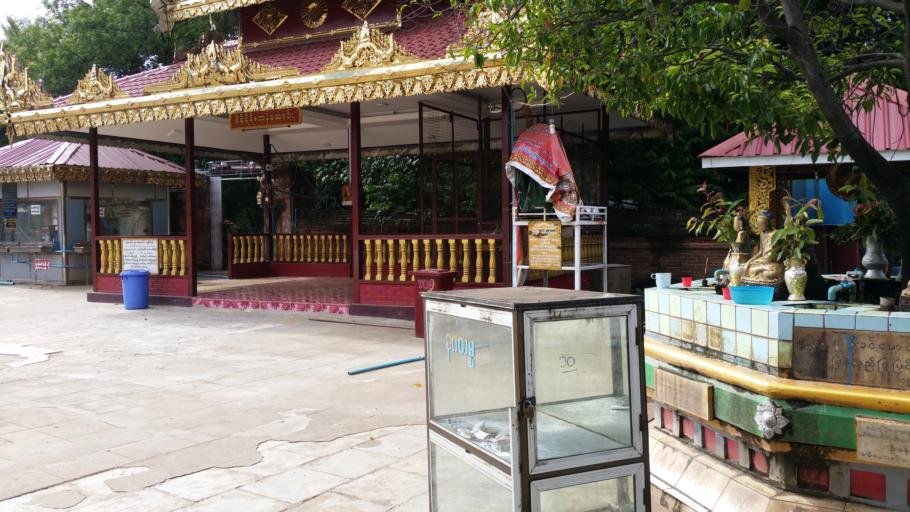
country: MM
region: Magway
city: Chauk
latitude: 21.1280
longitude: 94.8511
